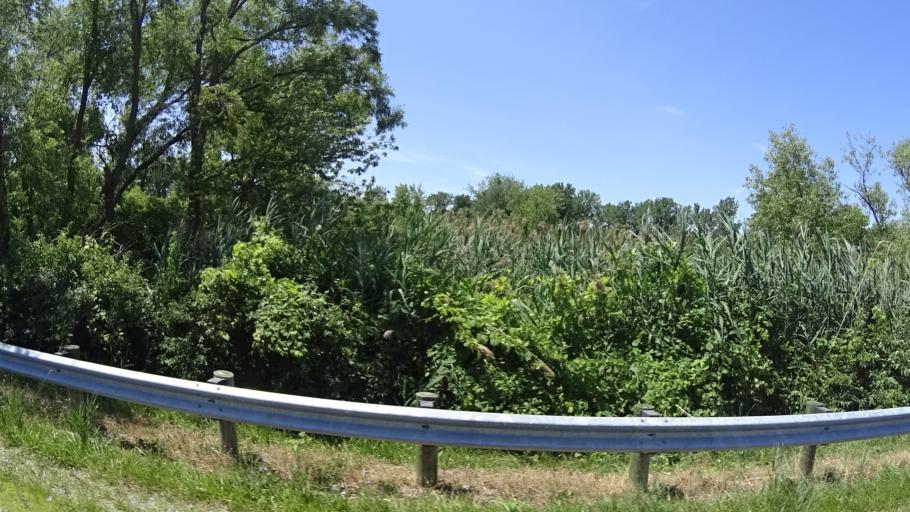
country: US
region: Ohio
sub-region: Erie County
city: Sandusky
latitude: 41.4538
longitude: -82.7825
